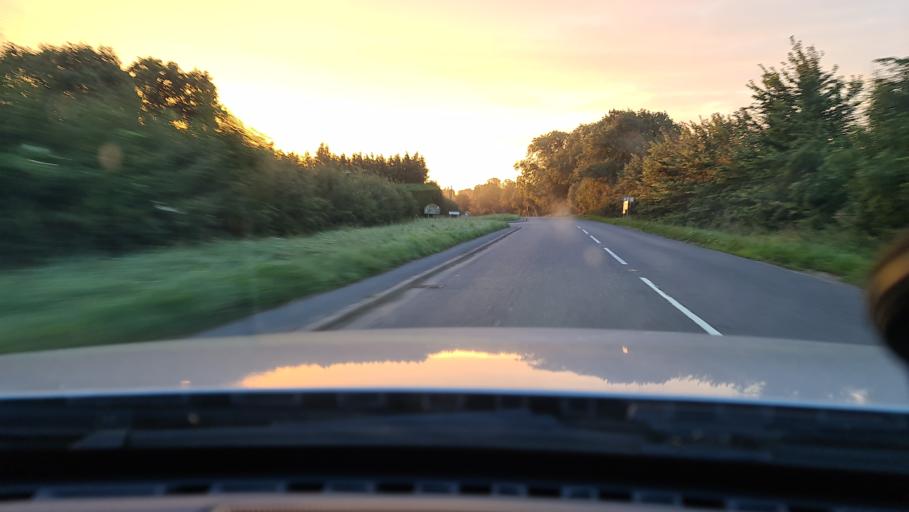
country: GB
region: England
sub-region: Leicestershire
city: Sapcote
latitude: 52.5385
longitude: -1.2979
